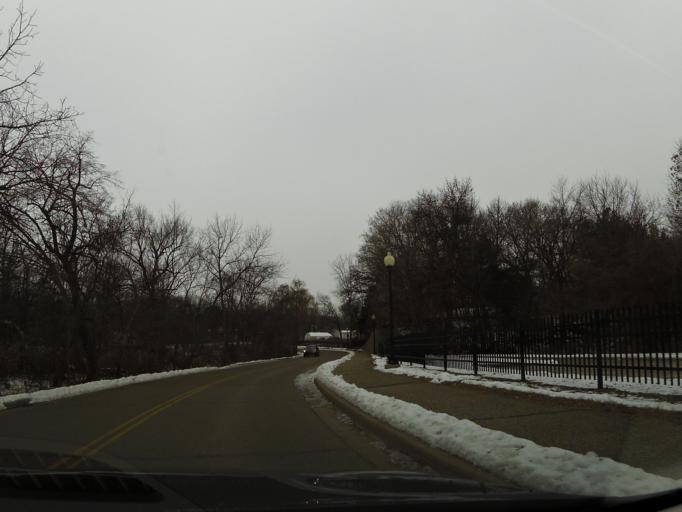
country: US
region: Minnesota
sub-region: Scott County
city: Jordan
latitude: 44.6594
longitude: -93.6299
